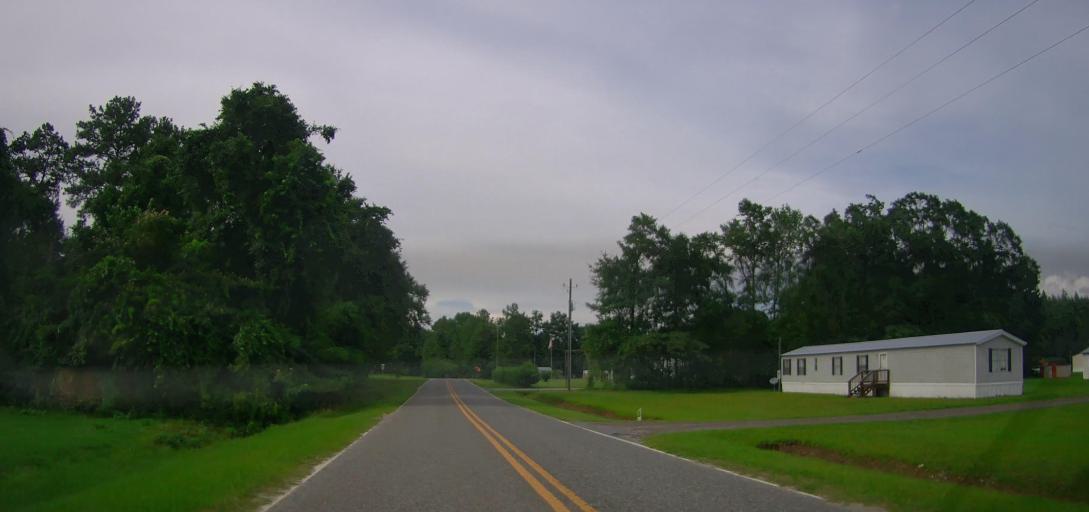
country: US
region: Georgia
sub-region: Wayne County
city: Jesup
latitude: 31.6750
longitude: -81.9073
